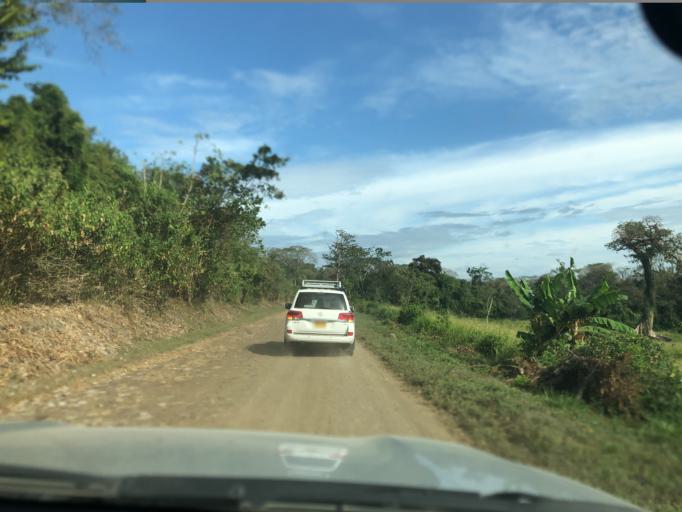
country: NI
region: Rivas
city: Cardenas
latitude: 11.1260
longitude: -85.2945
